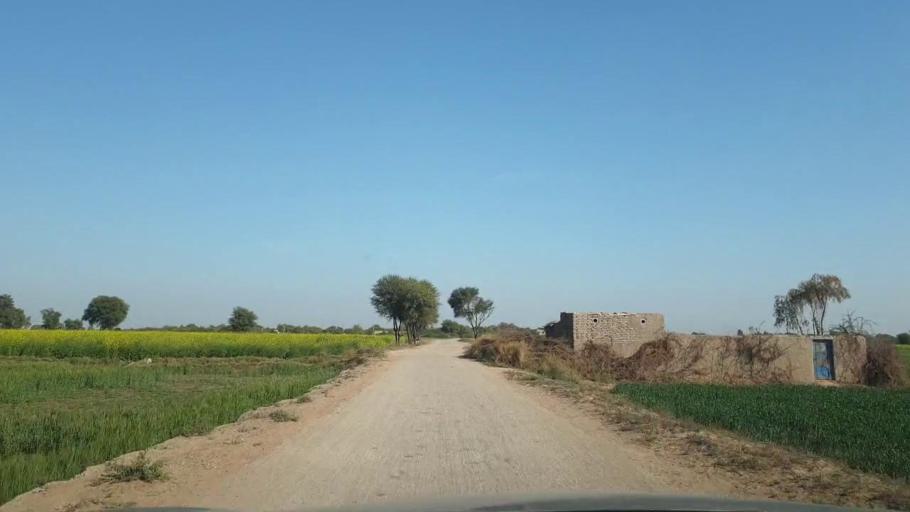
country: PK
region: Sindh
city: Tando Adam
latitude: 25.6876
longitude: 68.6750
